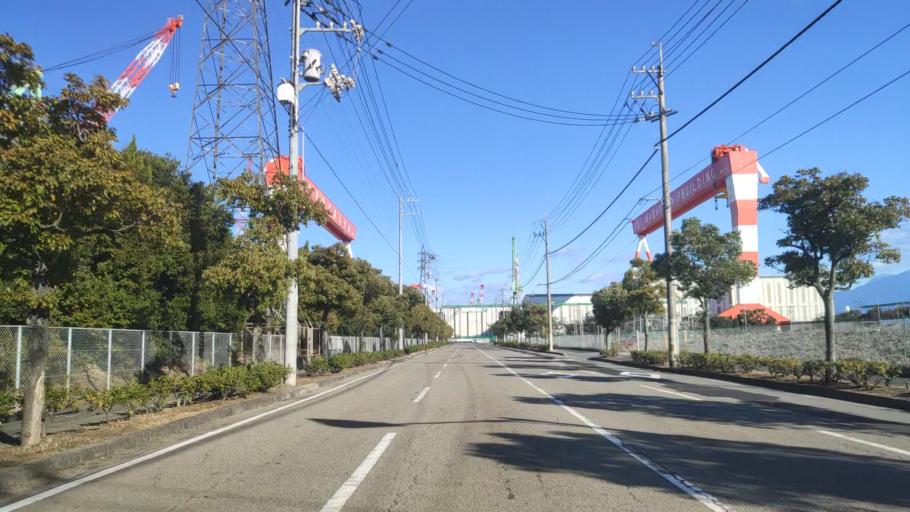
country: JP
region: Ehime
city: Saijo
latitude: 33.9399
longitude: 133.1884
